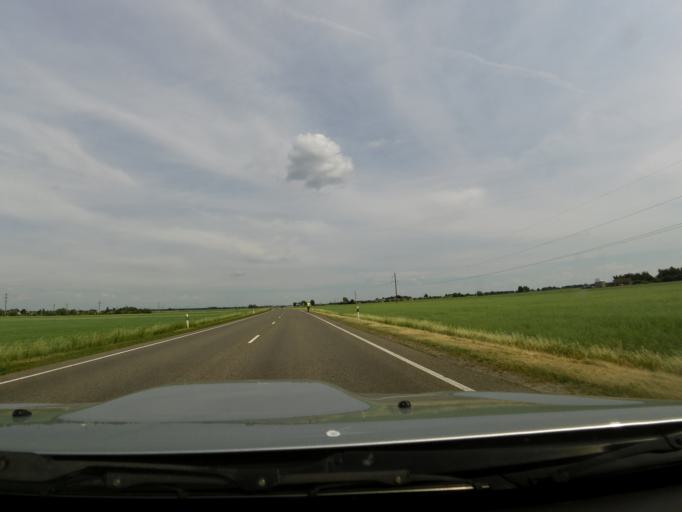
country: LT
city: Vilkaviskis
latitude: 54.6324
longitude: 23.0320
